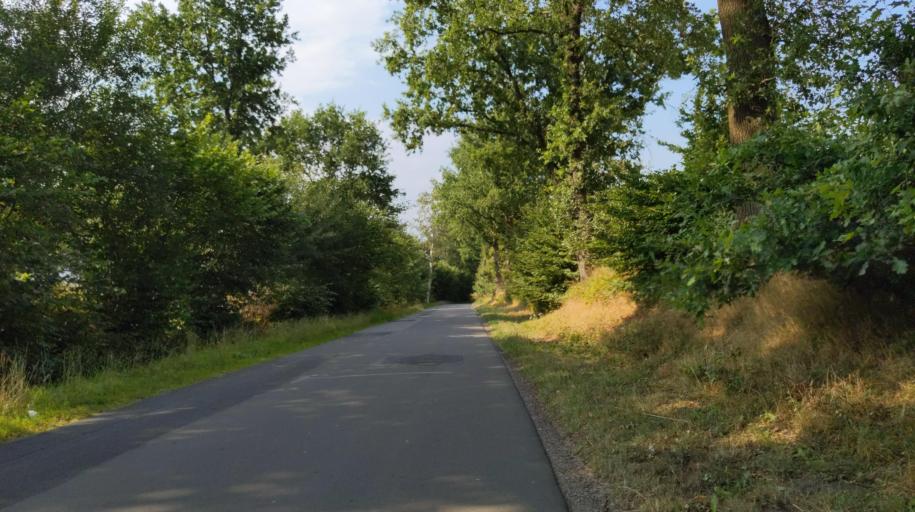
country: DE
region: Schleswig-Holstein
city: Rondeshagen
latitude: 53.7614
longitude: 10.6275
